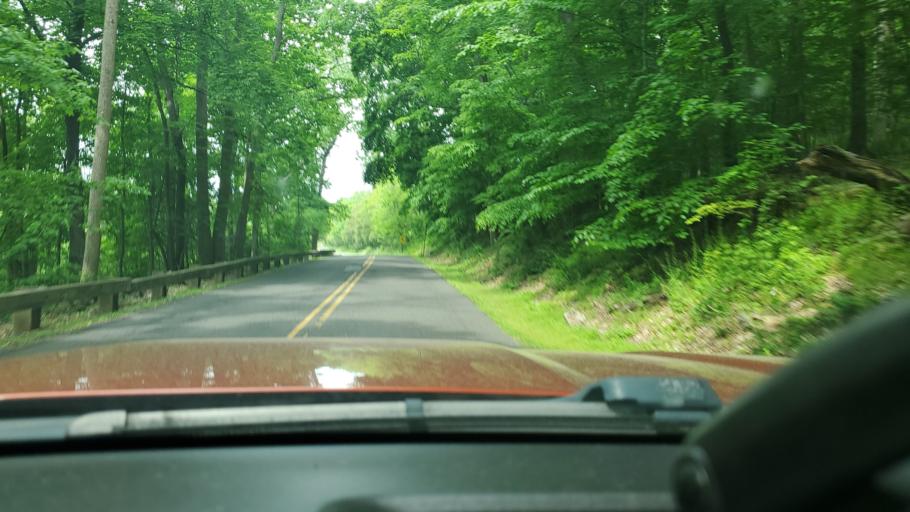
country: US
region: Pennsylvania
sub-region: Montgomery County
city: Red Hill
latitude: 40.3378
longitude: -75.4802
